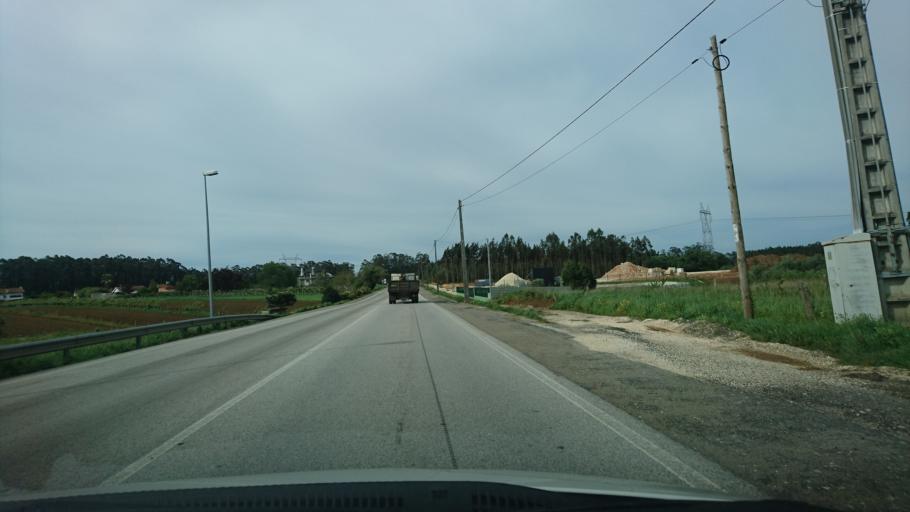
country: PT
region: Aveiro
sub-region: Albergaria-A-Velha
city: Albergaria-a-Velha
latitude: 40.6963
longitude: -8.5122
